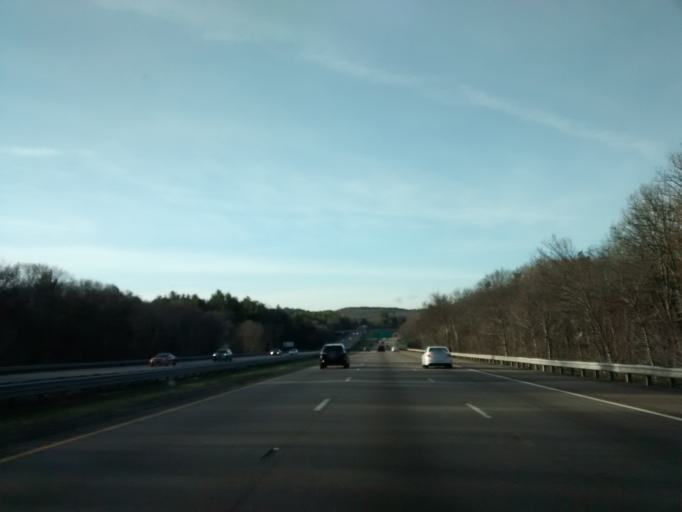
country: US
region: Massachusetts
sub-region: Norfolk County
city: Randolph
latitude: 42.1879
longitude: -71.0768
